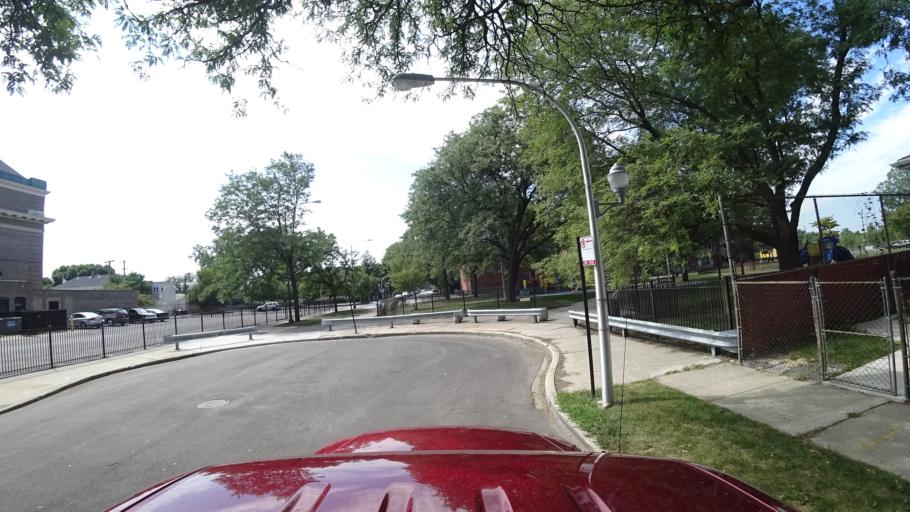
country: US
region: Illinois
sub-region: Cook County
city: Chicago
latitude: 41.8131
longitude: -87.6445
